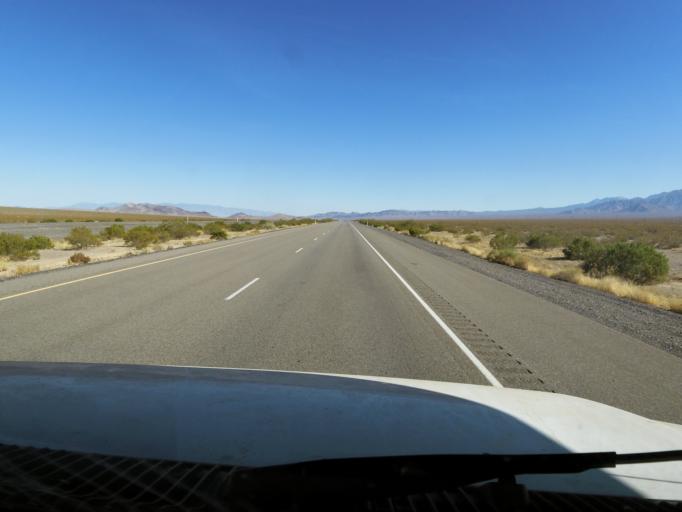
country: US
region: Nevada
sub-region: Nye County
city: Pahrump
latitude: 36.5967
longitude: -115.9519
